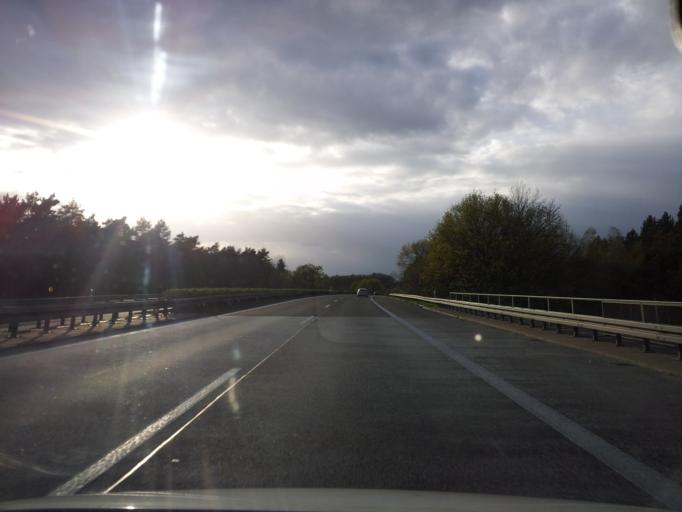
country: DE
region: Brandenburg
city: Lubbenau
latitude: 51.8352
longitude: 13.9689
